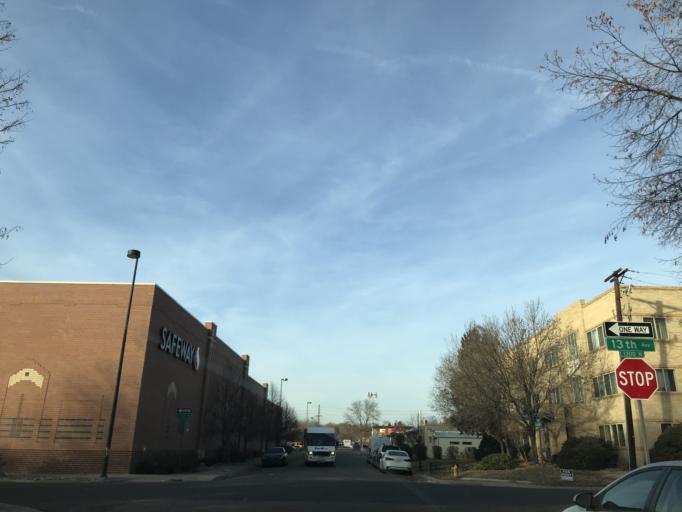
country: US
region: Colorado
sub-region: Arapahoe County
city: Glendale
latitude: 39.7366
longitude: -104.9150
